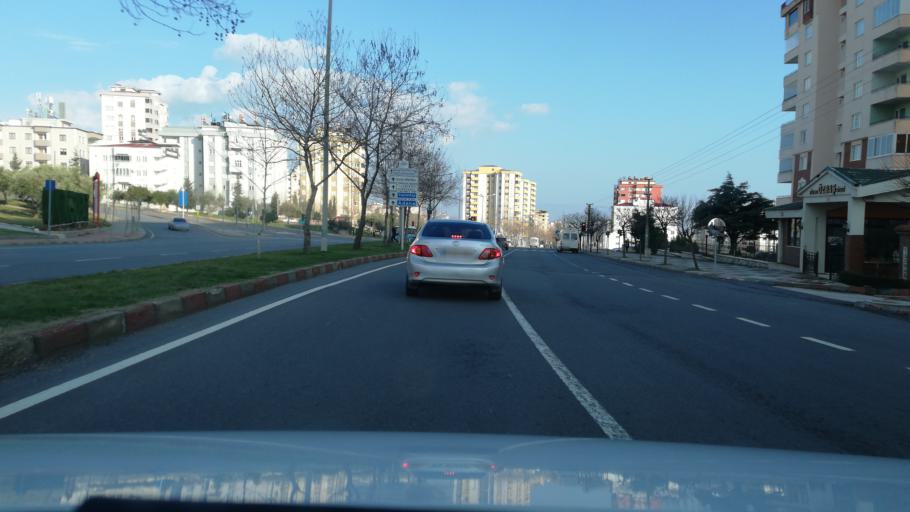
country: TR
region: Kahramanmaras
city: Kahramanmaras
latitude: 37.5954
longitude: 36.8899
